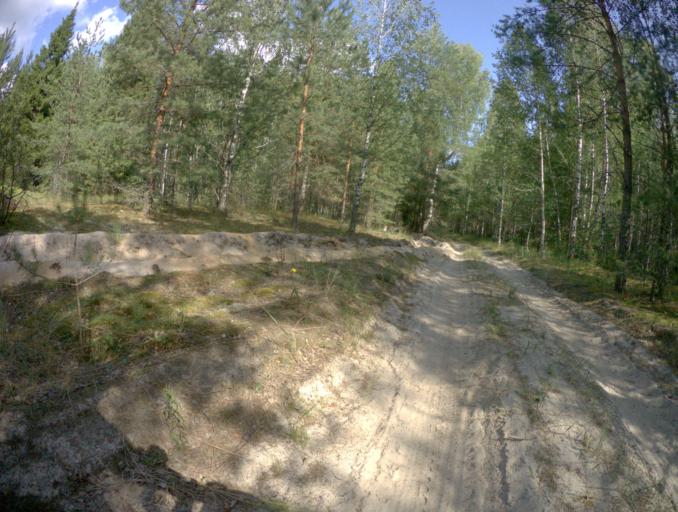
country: RU
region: Vladimir
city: Vorsha
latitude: 55.9093
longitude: 40.1640
